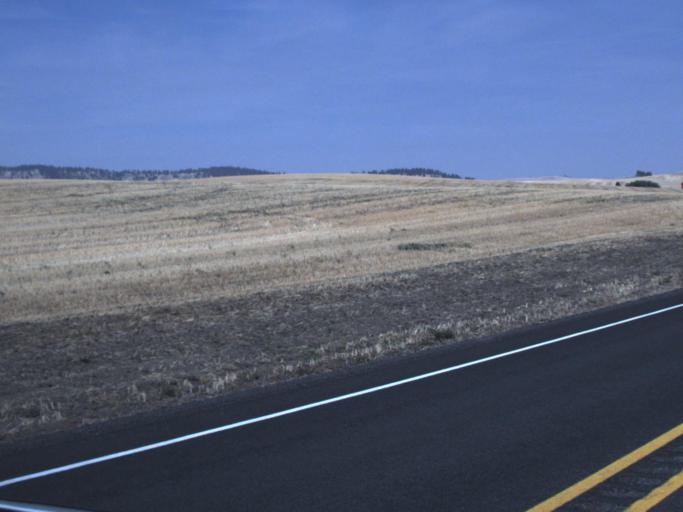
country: US
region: Washington
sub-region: Whitman County
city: Pullman
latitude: 46.8263
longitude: -117.1151
